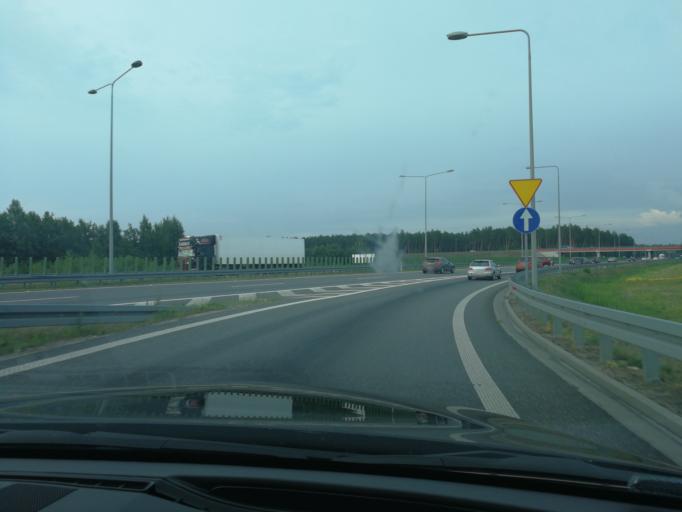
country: PL
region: Lodz Voivodeship
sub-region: powiat Lowicki
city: Nieborow
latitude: 52.0445
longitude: 20.0533
